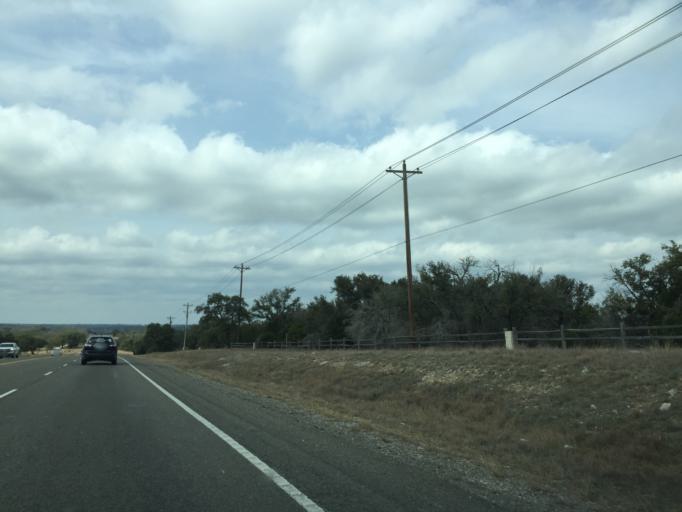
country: US
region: Texas
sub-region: Burnet County
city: Marble Falls
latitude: 30.4896
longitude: -98.2212
